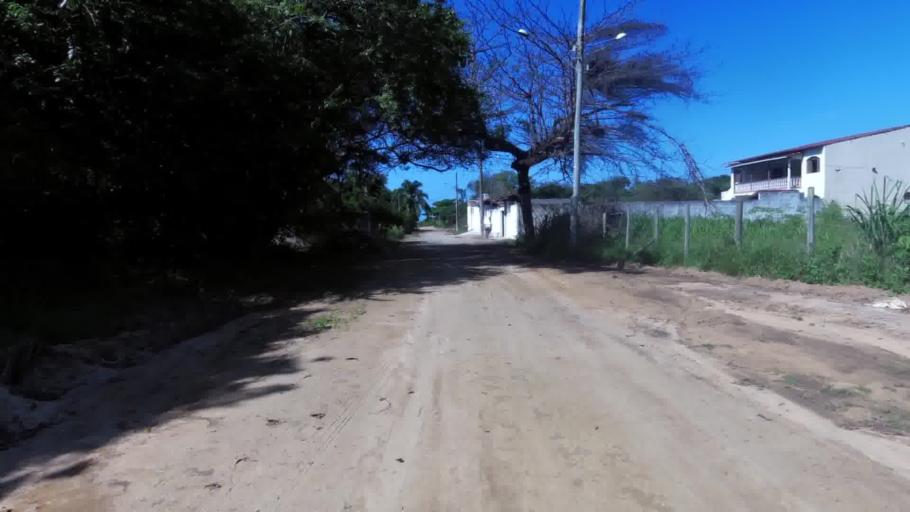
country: BR
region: Espirito Santo
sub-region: Piuma
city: Piuma
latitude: -20.8274
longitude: -40.6202
